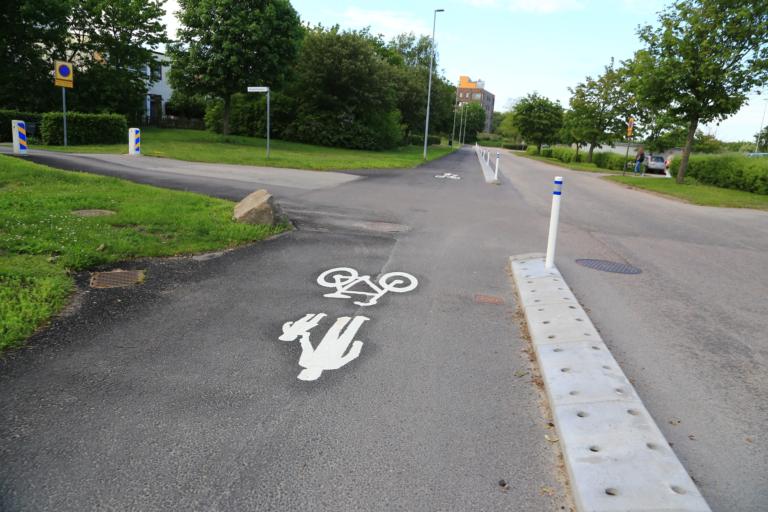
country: SE
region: Halland
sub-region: Varbergs Kommun
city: Varberg
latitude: 57.0930
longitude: 12.2669
